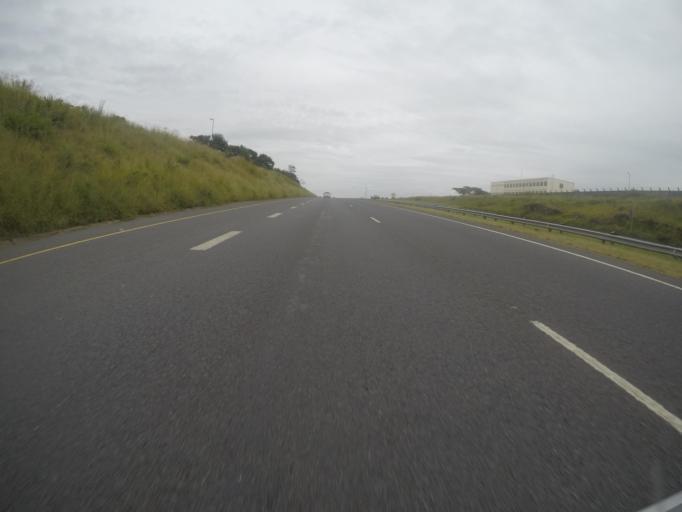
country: ZA
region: Eastern Cape
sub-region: Buffalo City Metropolitan Municipality
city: East London
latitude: -32.9721
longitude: 27.8914
